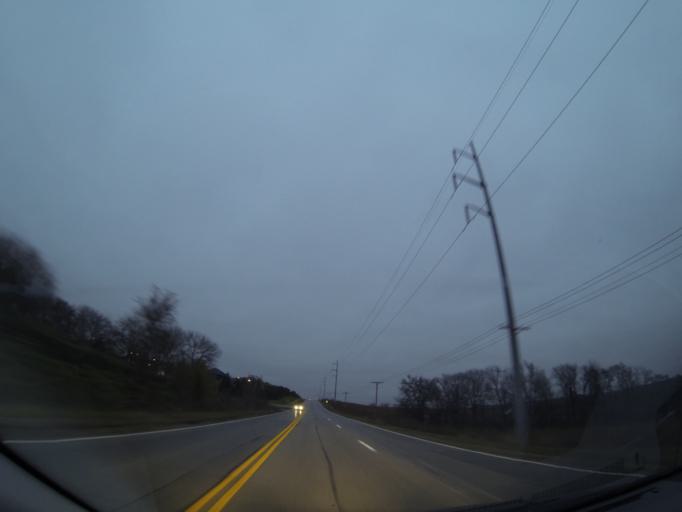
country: US
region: Nebraska
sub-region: Douglas County
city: Elkhorn
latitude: 41.2696
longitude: -96.1772
